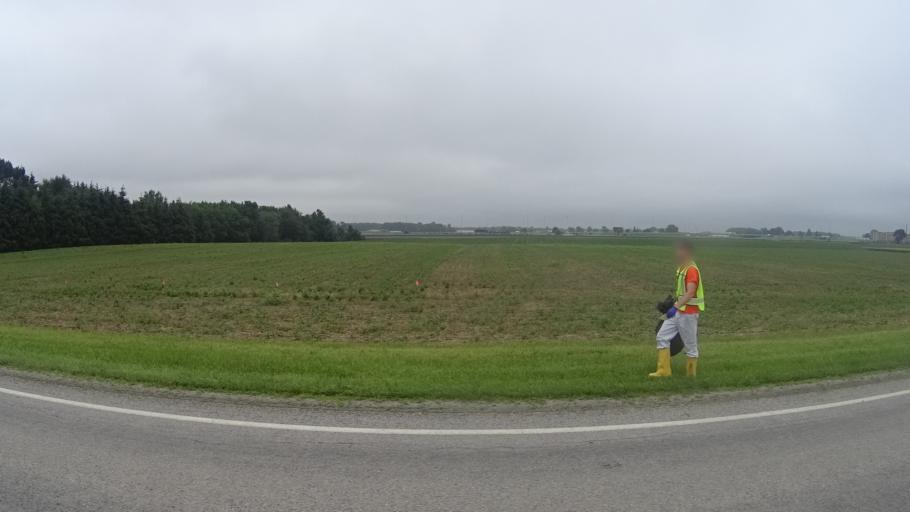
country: US
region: Ohio
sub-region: Erie County
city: Milan
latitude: 41.3325
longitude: -82.6121
